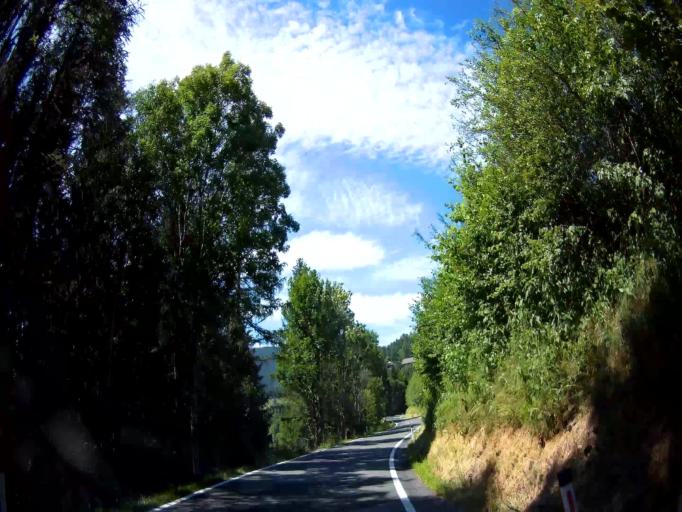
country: AT
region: Carinthia
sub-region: Politischer Bezirk Sankt Veit an der Glan
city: Glodnitz
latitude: 46.9112
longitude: 14.0923
